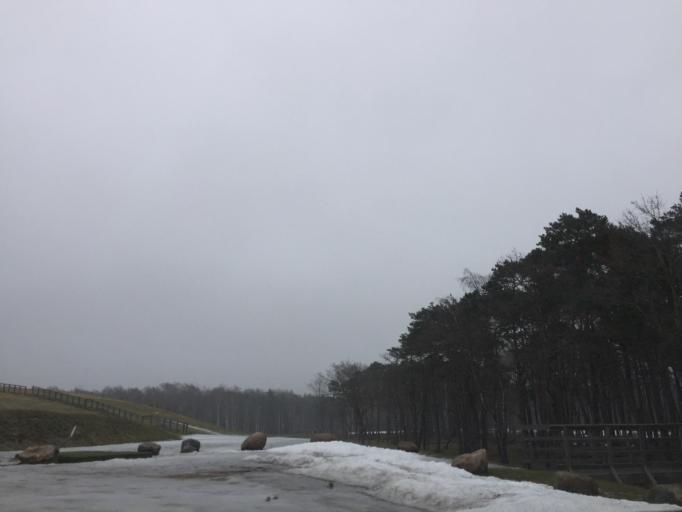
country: EE
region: Saare
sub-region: Kuressaare linn
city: Kuressaare
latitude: 58.2673
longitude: 22.5383
